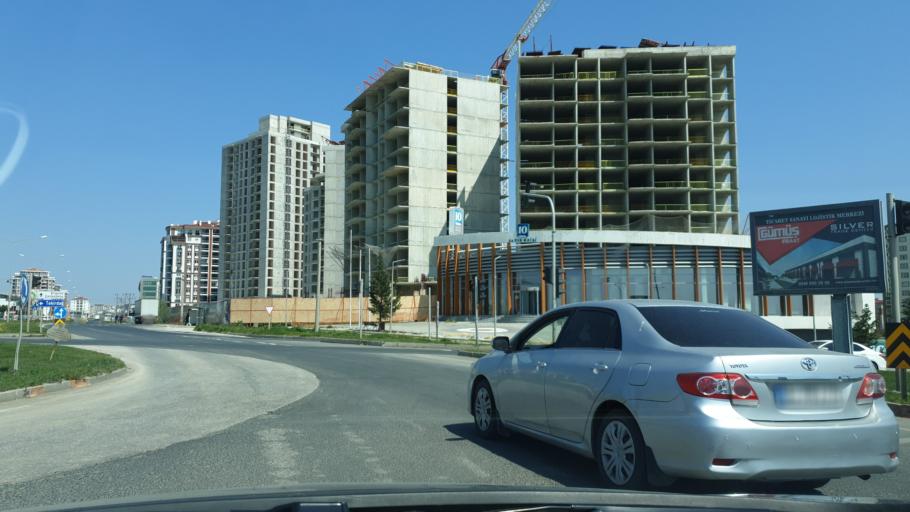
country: TR
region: Tekirdag
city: Corlu
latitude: 41.1497
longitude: 27.7767
